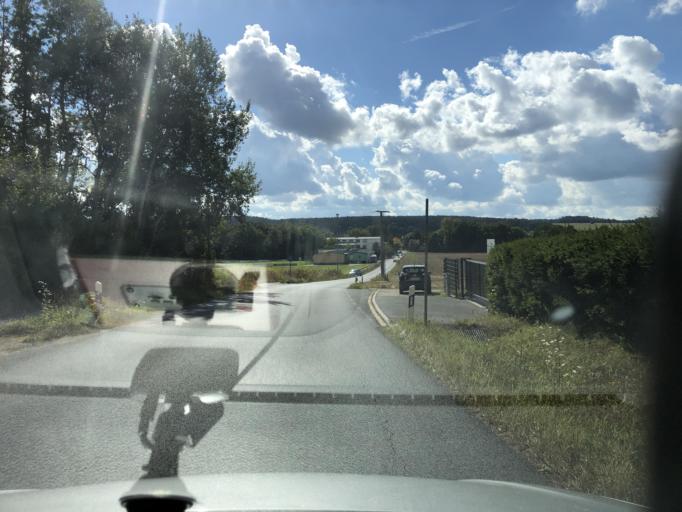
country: DE
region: Bavaria
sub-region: Regierungsbezirk Mittelfranken
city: Zirndorf
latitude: 49.4329
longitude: 10.9123
